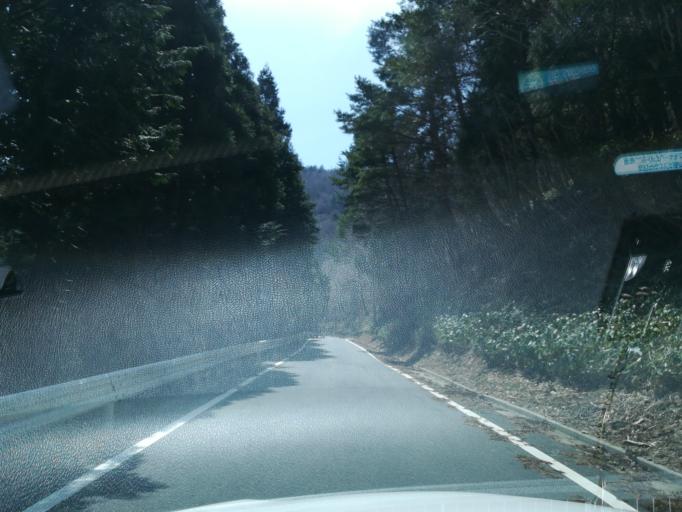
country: JP
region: Tokushima
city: Wakimachi
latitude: 33.8764
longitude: 134.0591
